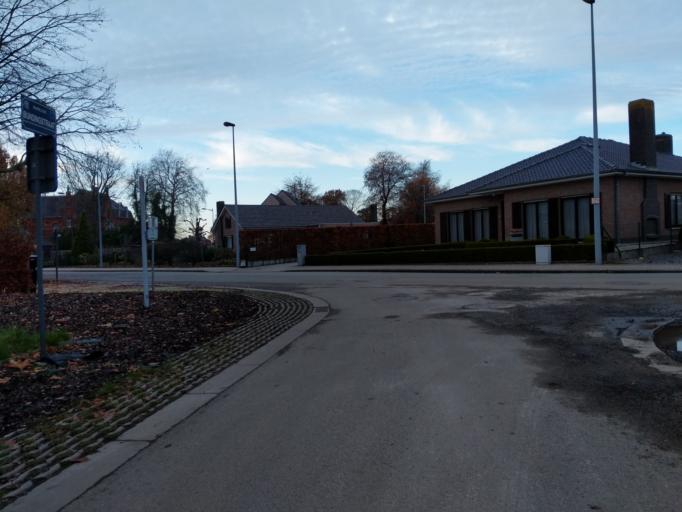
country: BE
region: Flanders
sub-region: Provincie West-Vlaanderen
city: Ruiselede
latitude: 51.0381
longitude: 3.3981
